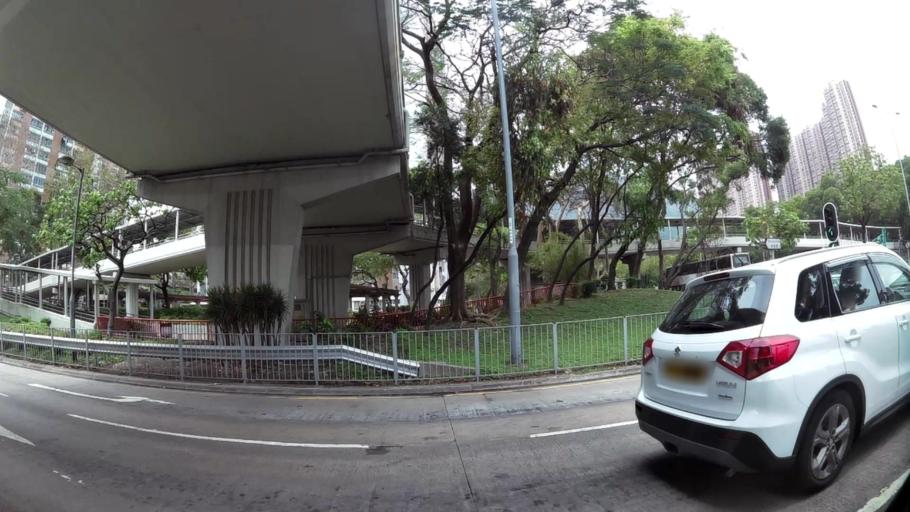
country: HK
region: Tuen Mun
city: Tuen Mun
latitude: 22.3775
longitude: 113.9665
